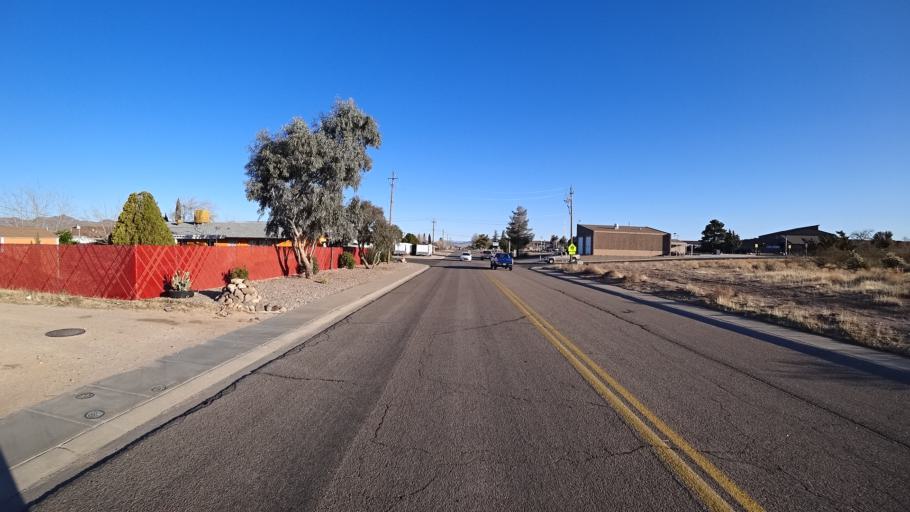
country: US
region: Arizona
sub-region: Mohave County
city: Kingman
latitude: 35.1917
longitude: -114.0115
